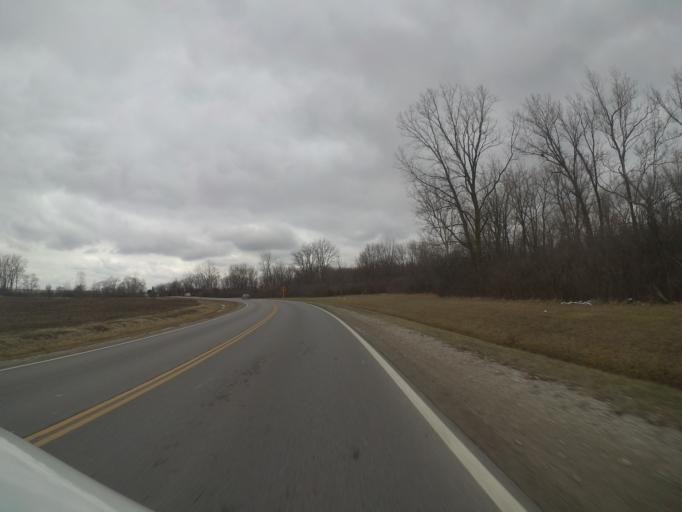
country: US
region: Ohio
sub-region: Wood County
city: Walbridge
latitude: 41.6080
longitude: -83.5178
